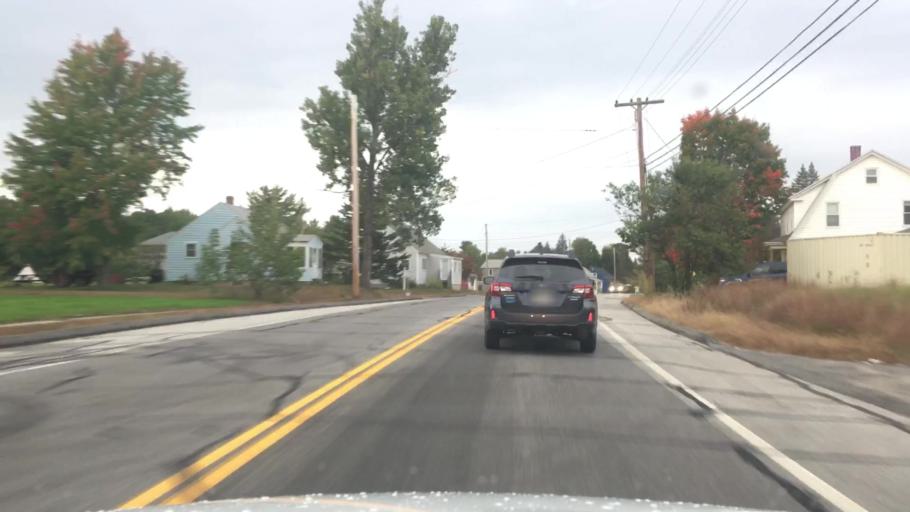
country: US
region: Maine
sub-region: York County
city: Waterboro
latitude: 43.5311
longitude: -70.7187
